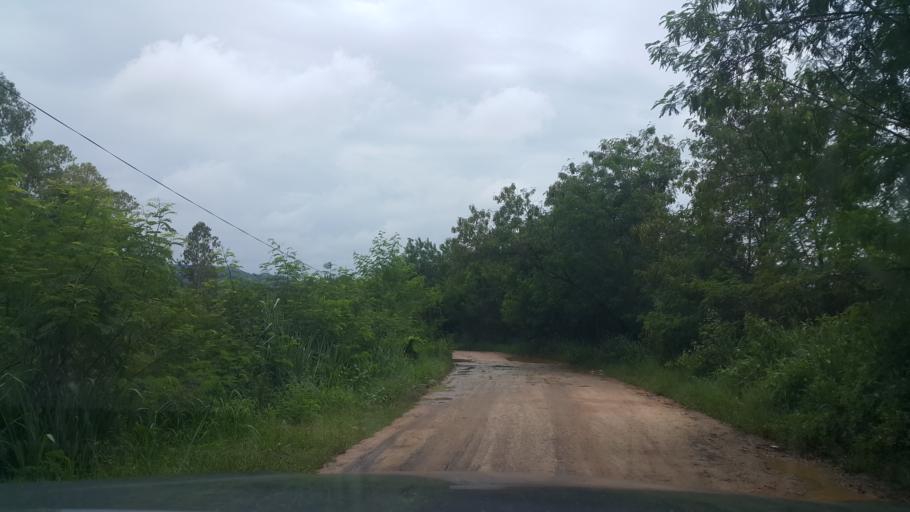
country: TH
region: Chiang Mai
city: San Sai
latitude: 18.9117
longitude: 99.0588
